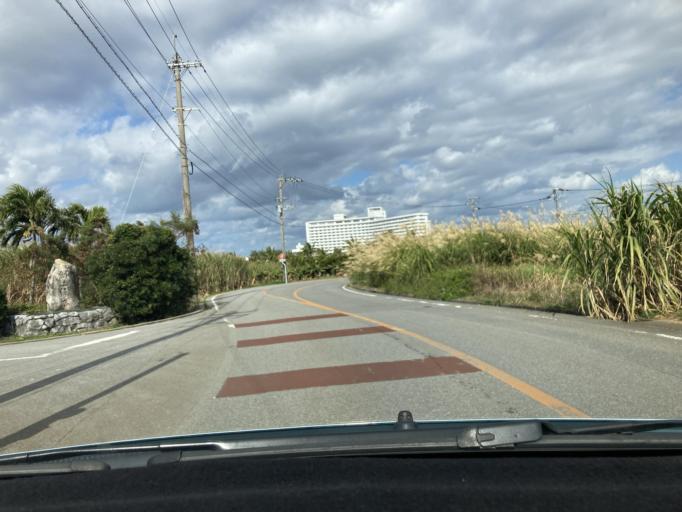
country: JP
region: Okinawa
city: Ishikawa
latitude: 26.4301
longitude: 127.7188
